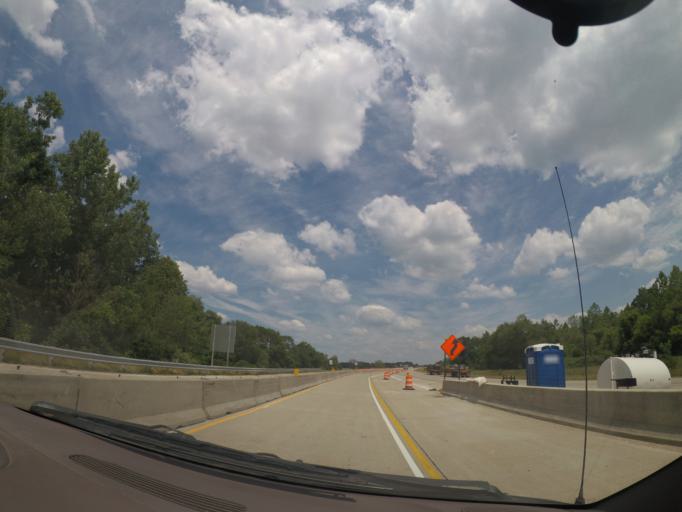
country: US
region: Indiana
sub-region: Elkhart County
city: Dunlap
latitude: 41.6567
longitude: -85.9303
